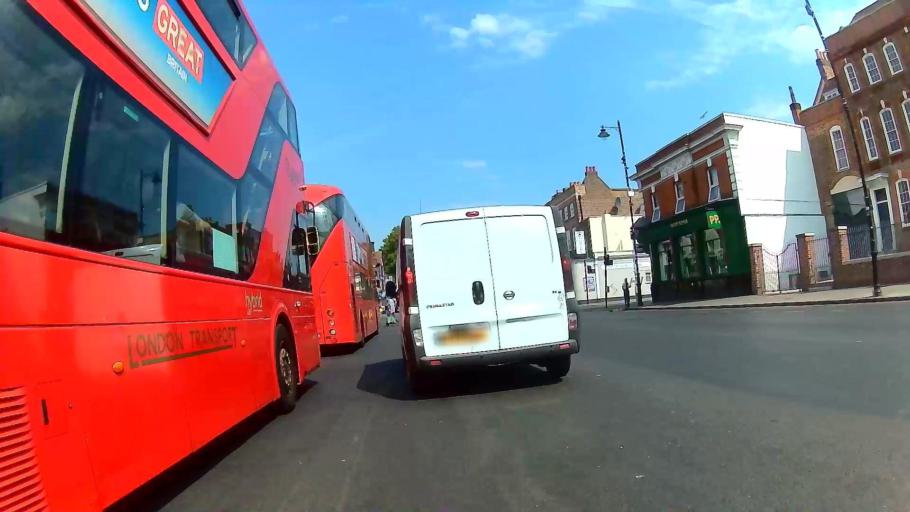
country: GB
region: England
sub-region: Greater London
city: Harringay
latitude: 51.6060
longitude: -0.0682
